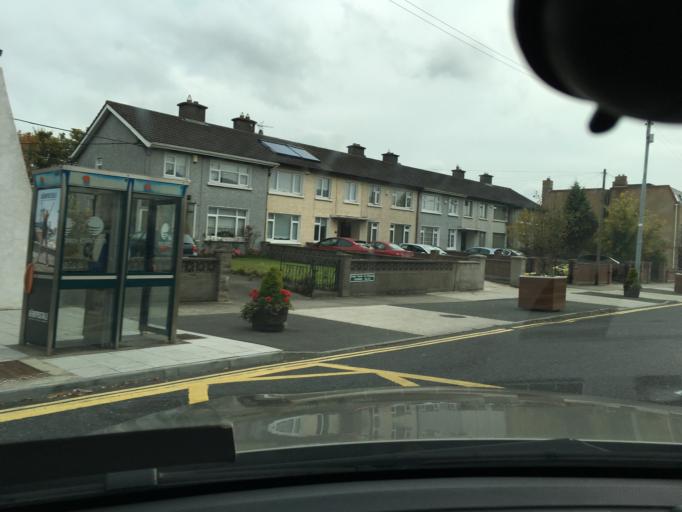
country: IE
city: Palmerstown
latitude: 53.3560
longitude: -6.3706
